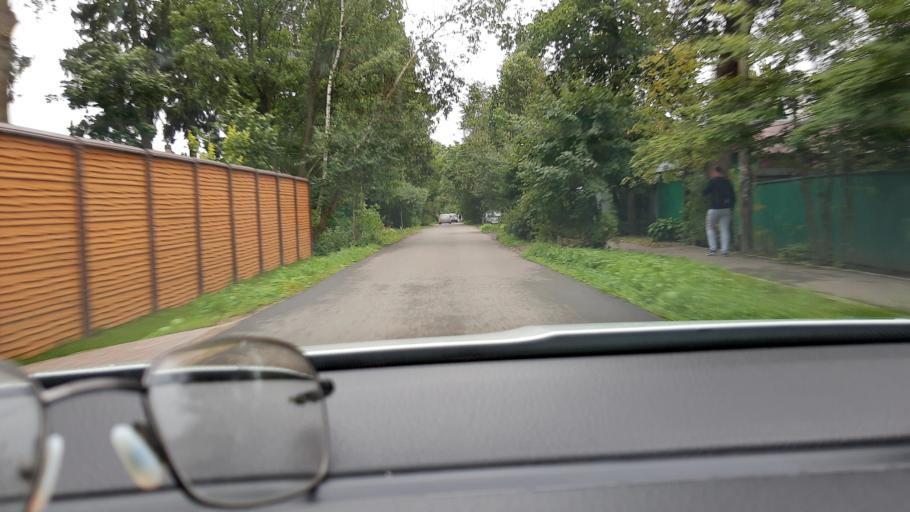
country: RU
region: Moskovskaya
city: Kokoshkino
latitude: 55.5957
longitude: 37.1723
